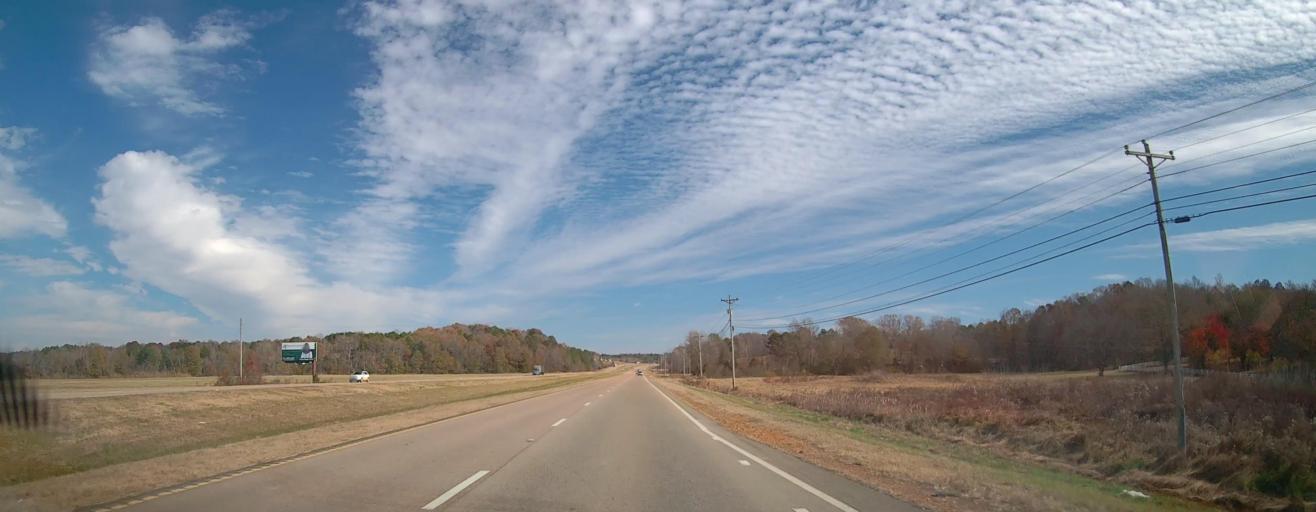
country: US
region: Mississippi
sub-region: Tippah County
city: Ripley
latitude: 34.9541
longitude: -88.8669
